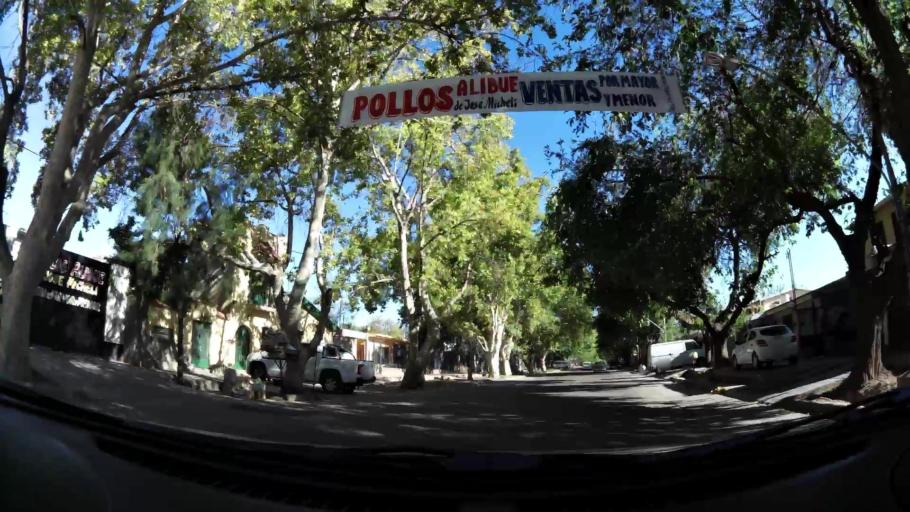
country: AR
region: Mendoza
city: Las Heras
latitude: -32.8559
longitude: -68.8270
